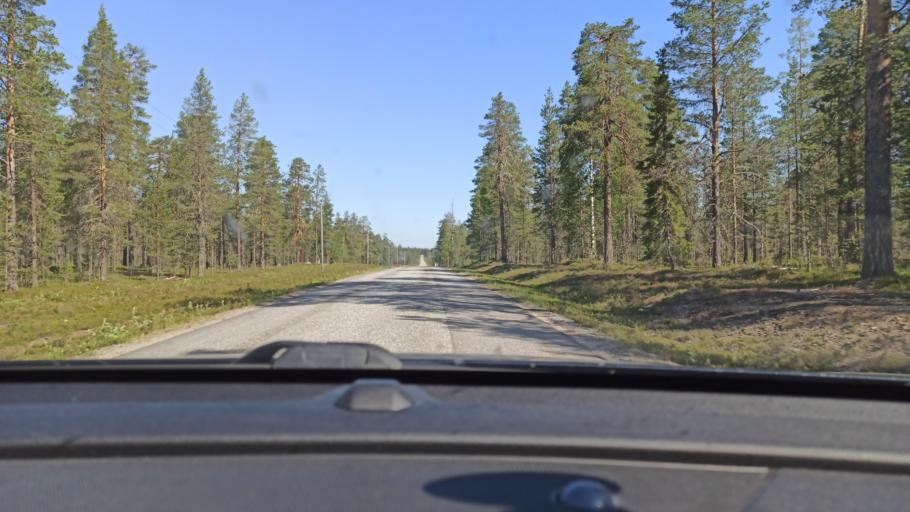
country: FI
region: Lapland
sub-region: Tunturi-Lappi
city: Kolari
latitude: 67.6420
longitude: 24.1584
